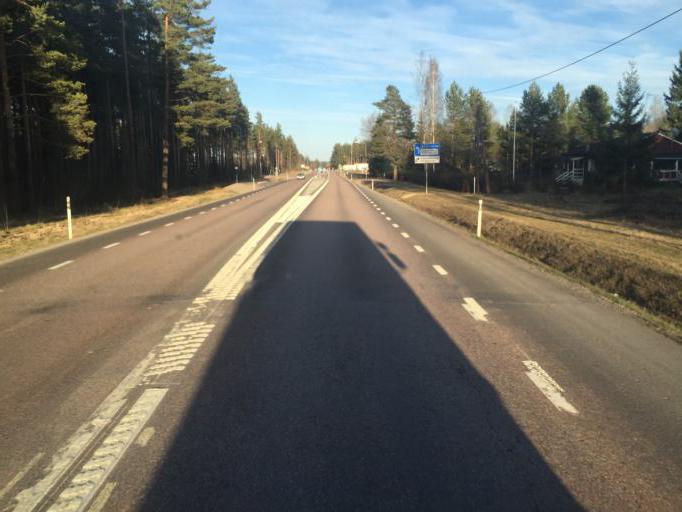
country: SE
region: Dalarna
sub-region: Borlange Kommun
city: Borlaenge
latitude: 60.5296
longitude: 15.3280
